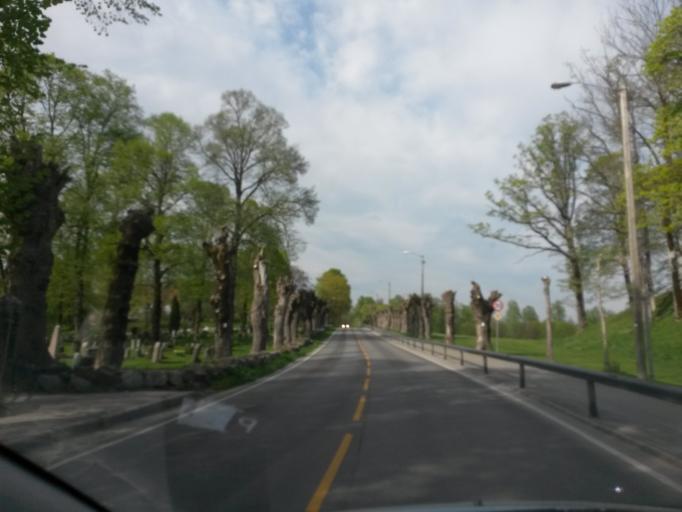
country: NO
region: Akershus
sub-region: Asker
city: Asker
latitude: 59.8433
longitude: 10.4379
